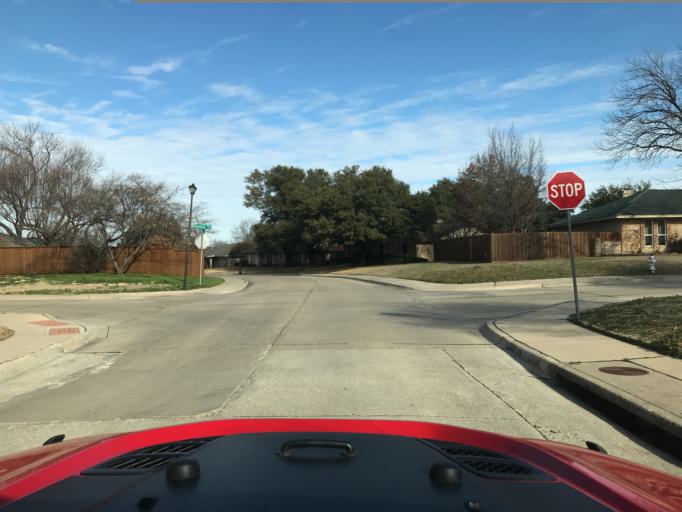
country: US
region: Texas
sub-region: Denton County
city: Lewisville
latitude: 33.0500
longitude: -97.0324
